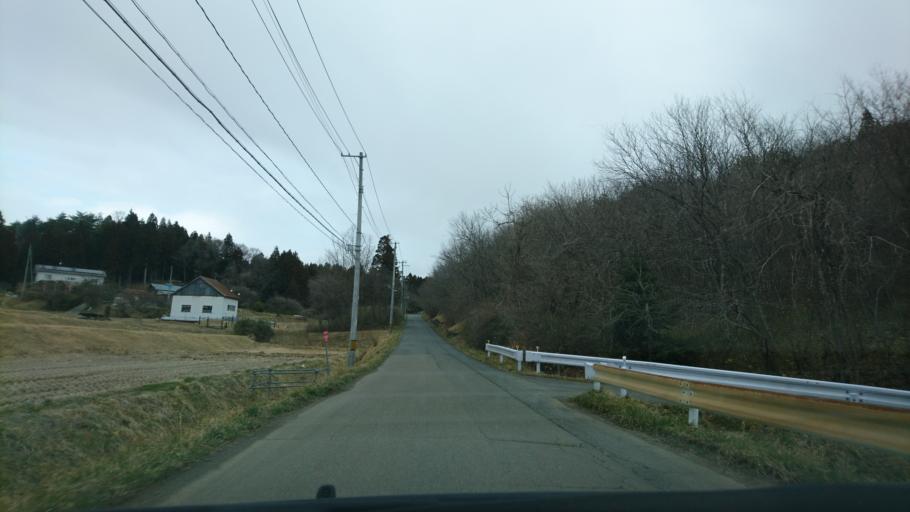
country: JP
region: Iwate
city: Ichinoseki
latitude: 38.8270
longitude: 141.1745
